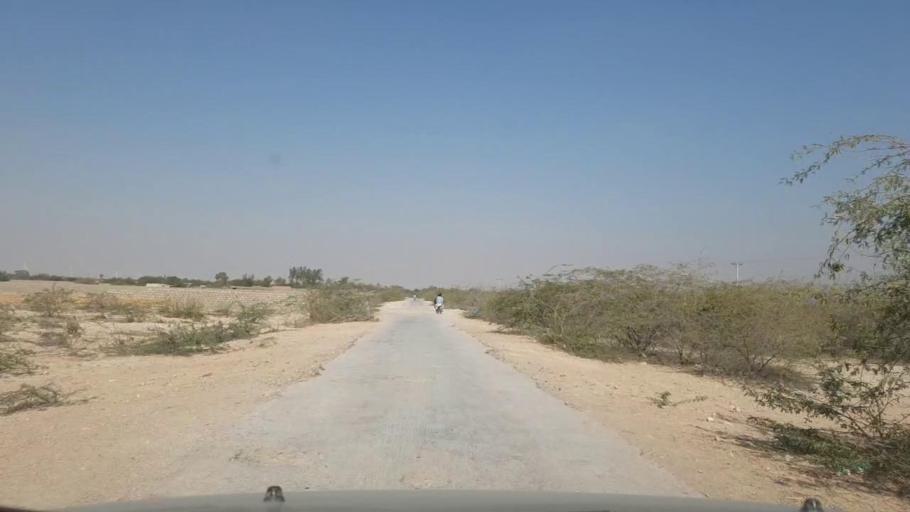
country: PK
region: Sindh
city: Daro Mehar
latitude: 25.0099
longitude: 68.0147
